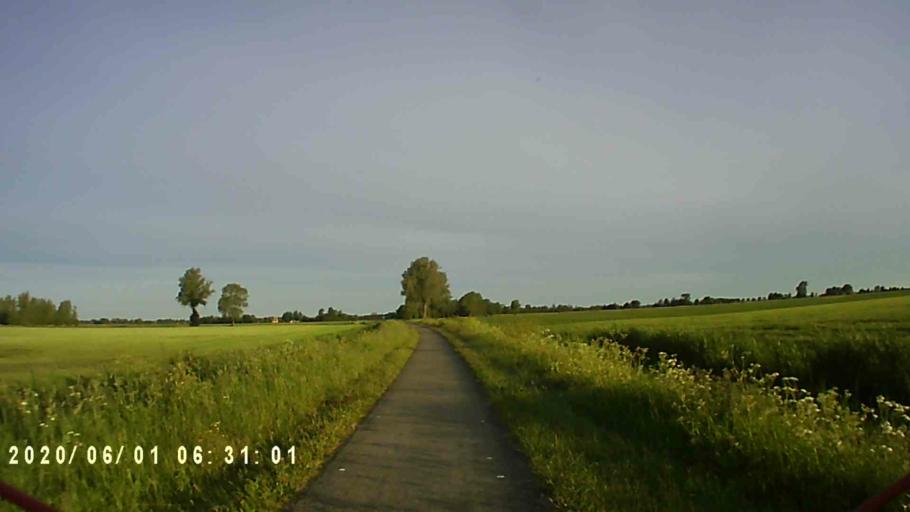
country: NL
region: Friesland
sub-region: Gemeente Kollumerland en Nieuwkruisland
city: Kollum
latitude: 53.2721
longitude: 6.1813
